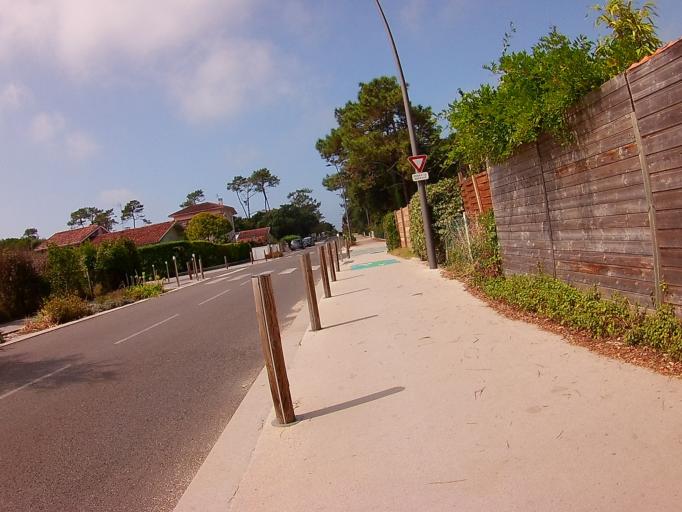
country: FR
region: Aquitaine
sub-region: Departement des Landes
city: Ondres
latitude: 43.5965
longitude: -1.4648
